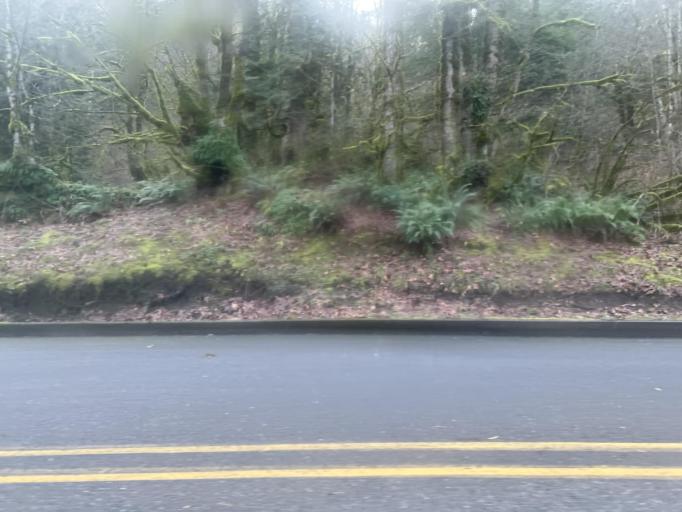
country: US
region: Washington
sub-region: Clark County
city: Washougal
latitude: 45.5328
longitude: -122.2347
